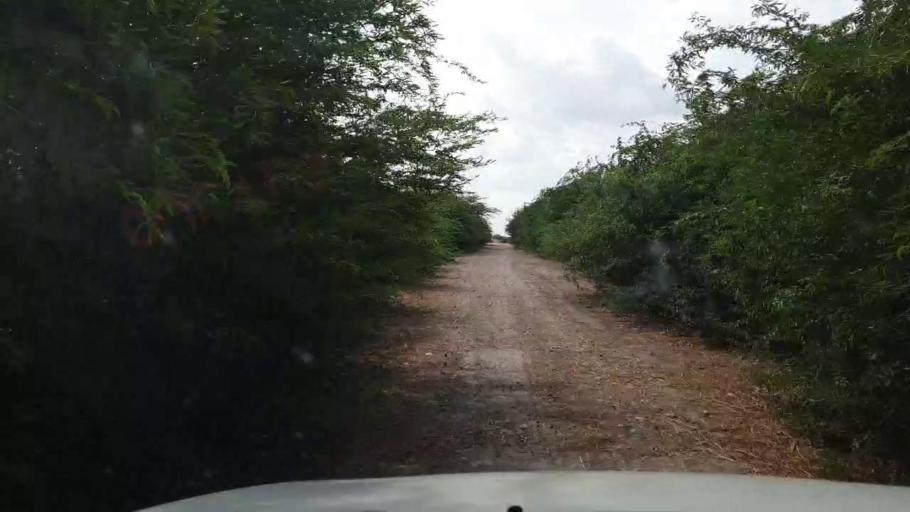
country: PK
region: Sindh
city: Kario
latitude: 24.6997
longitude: 68.6452
